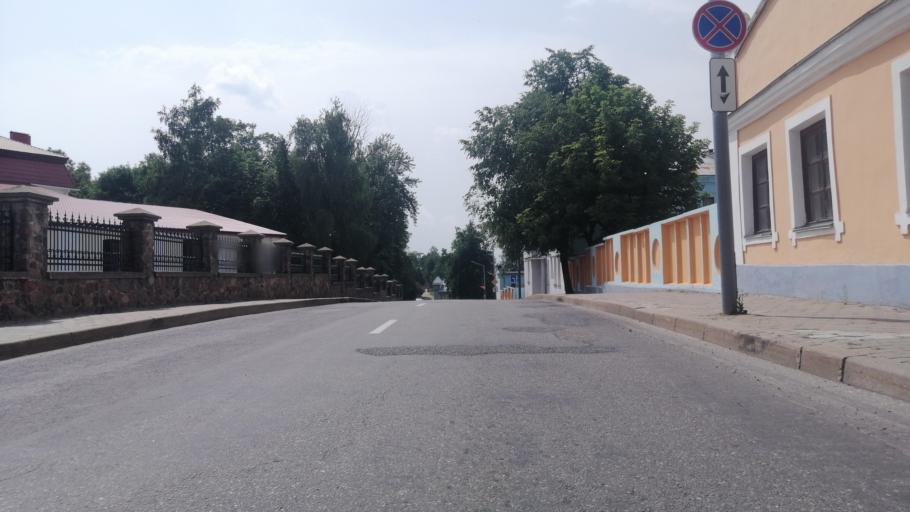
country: BY
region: Grodnenskaya
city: Navahrudak
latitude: 53.5976
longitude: 25.8242
